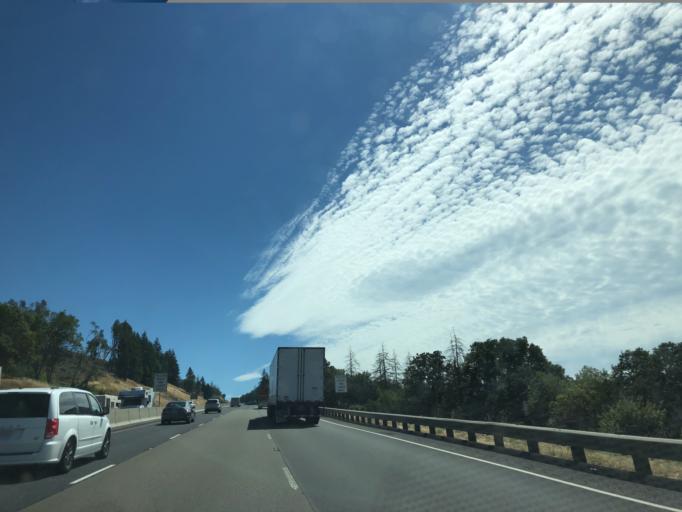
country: US
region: Oregon
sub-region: Douglas County
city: Sutherlin
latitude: 43.4112
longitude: -123.3294
